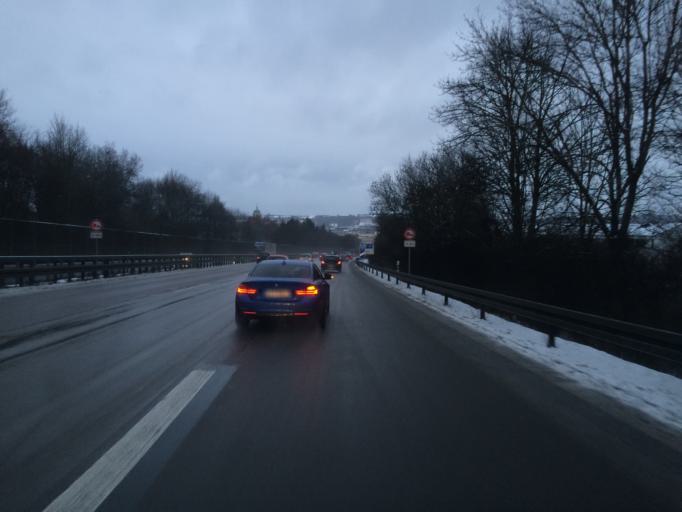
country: DE
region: Bavaria
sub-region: Upper Palatinate
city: Pentling
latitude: 49.0048
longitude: 12.0616
